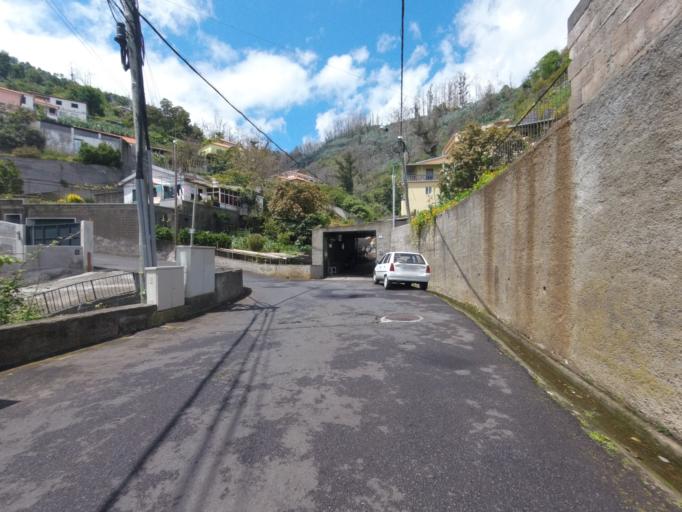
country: PT
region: Madeira
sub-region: Funchal
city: Nossa Senhora do Monte
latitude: 32.6756
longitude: -16.9232
